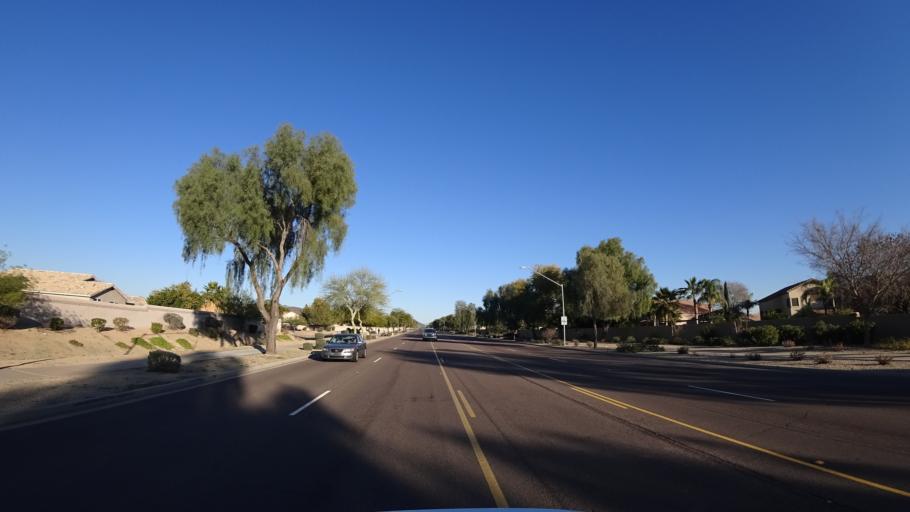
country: US
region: Arizona
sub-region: Maricopa County
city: Sun City
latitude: 33.6817
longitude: -112.2190
